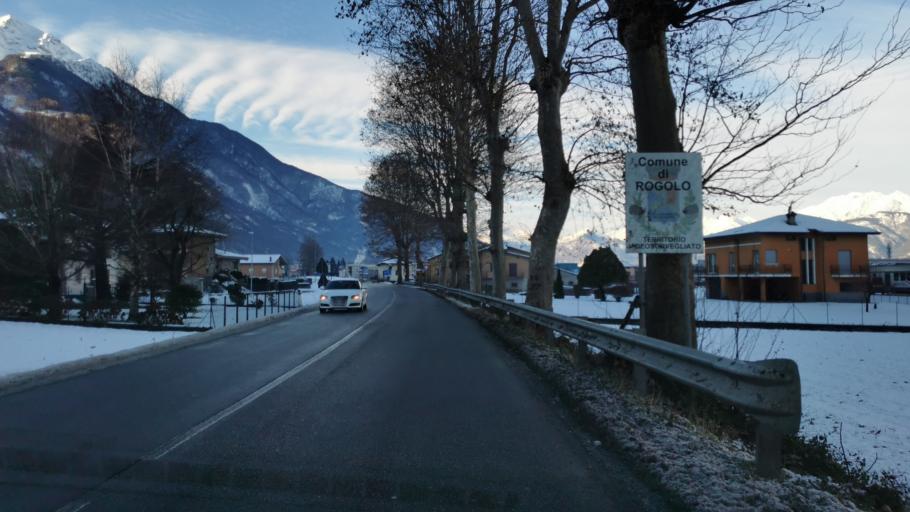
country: IT
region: Lombardy
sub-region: Provincia di Sondrio
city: Rogolo
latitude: 46.1383
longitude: 9.4912
